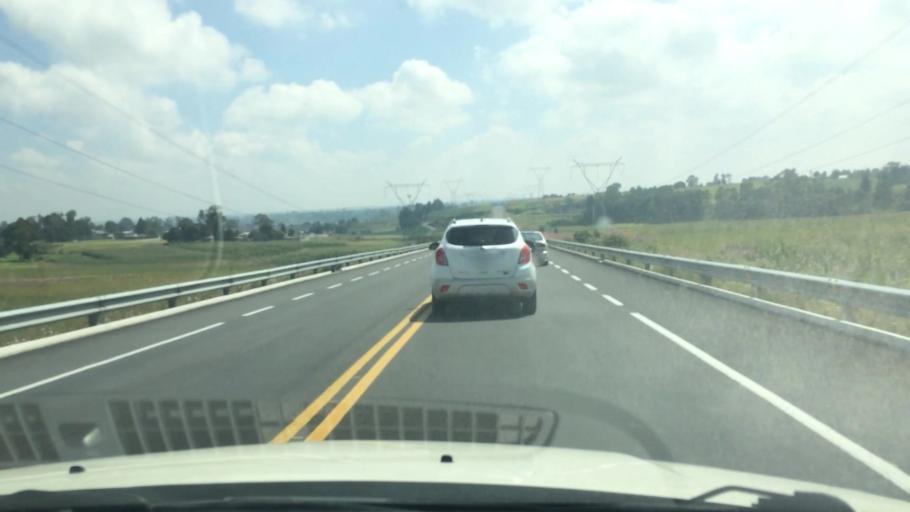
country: MX
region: Mexico
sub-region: Almoloya de Juarez
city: San Pedro de la Hortaliza (Ejido Almoloyan)
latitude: 19.3779
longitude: -99.8430
